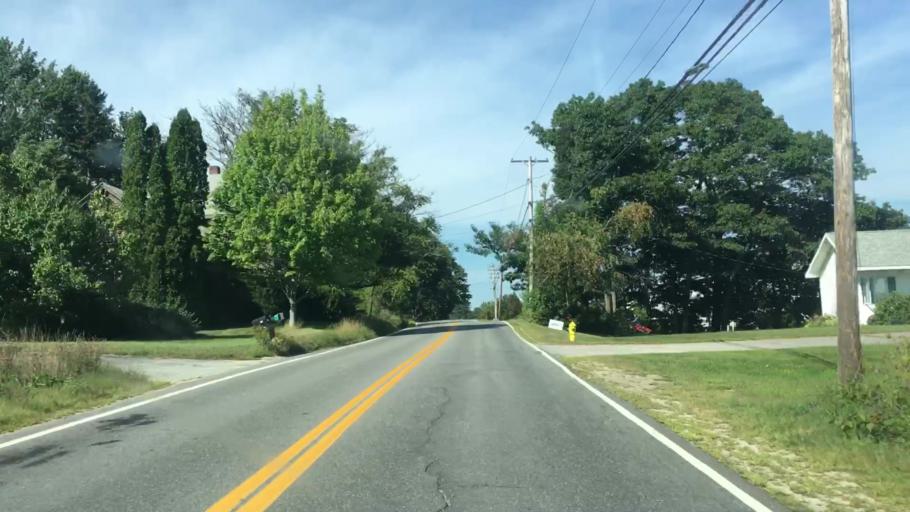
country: US
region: Maine
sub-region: Sagadahoc County
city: Bath
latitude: 43.9244
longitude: -69.8592
